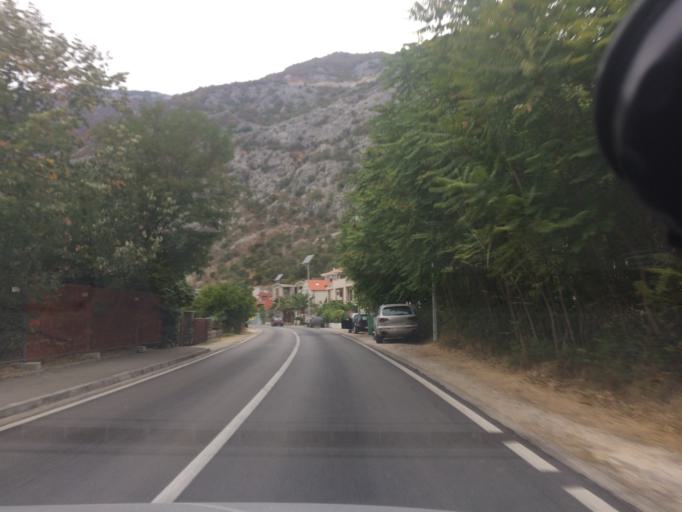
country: ME
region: Kotor
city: Risan
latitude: 42.5168
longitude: 18.6917
